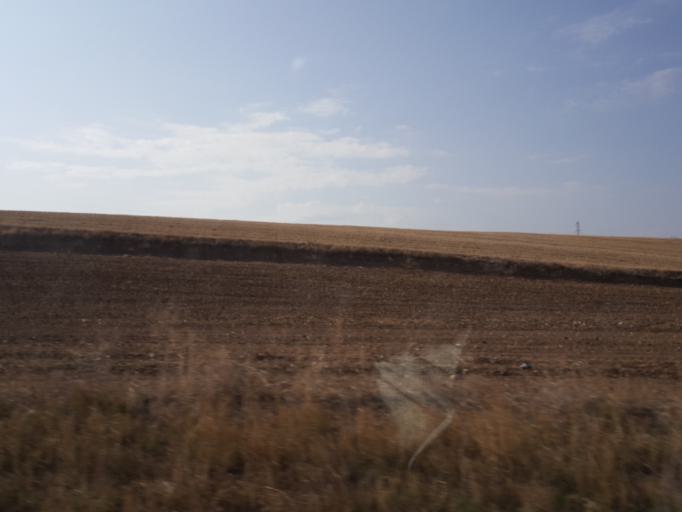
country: TR
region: Corum
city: Cemilbey
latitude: 40.1762
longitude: 35.0353
